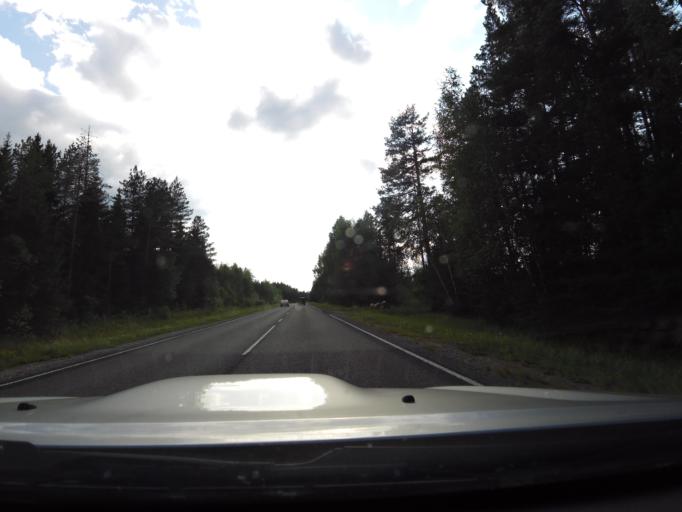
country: LT
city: Juodupe
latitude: 56.2019
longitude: 25.5766
